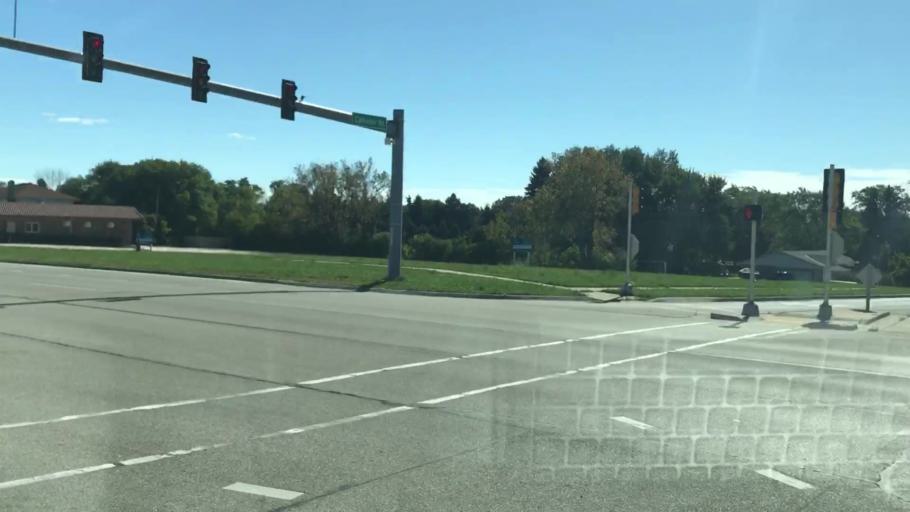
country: US
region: Wisconsin
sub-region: Waukesha County
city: Brookfield
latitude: 43.0900
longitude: -88.1255
